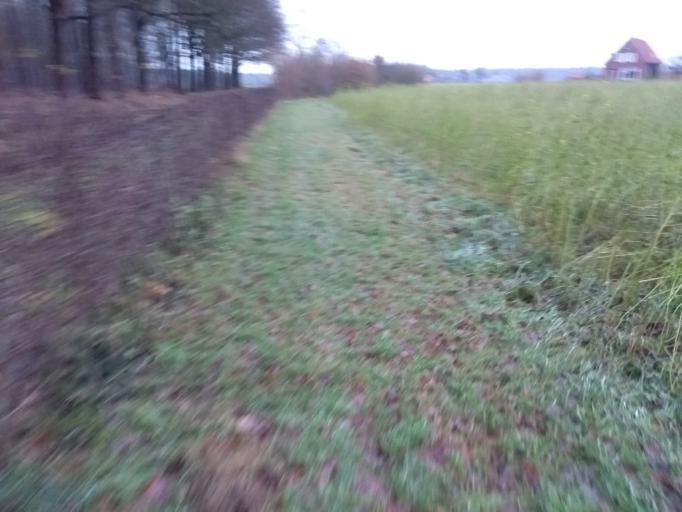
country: NL
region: Gelderland
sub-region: Gemeente Bronckhorst
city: Zelhem
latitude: 52.0407
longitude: 6.3479
